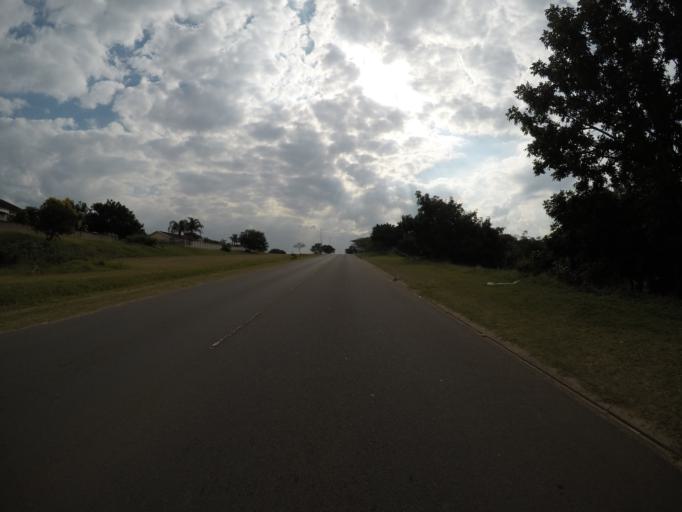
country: ZA
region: KwaZulu-Natal
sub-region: uThungulu District Municipality
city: Richards Bay
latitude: -28.7439
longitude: 32.0832
